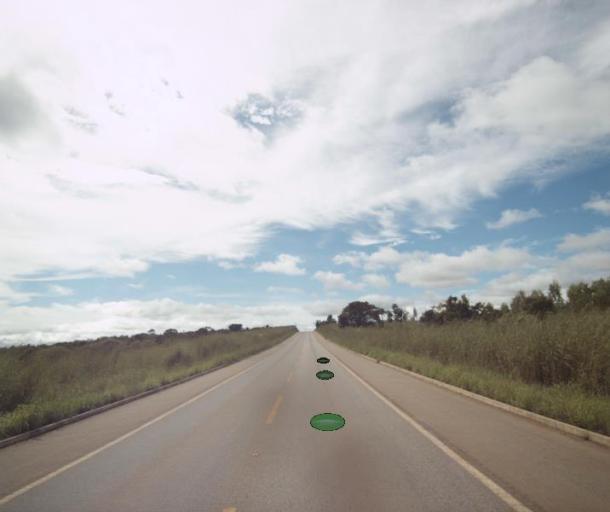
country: BR
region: Goias
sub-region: Barro Alto
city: Barro Alto
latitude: -15.2068
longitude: -48.7151
